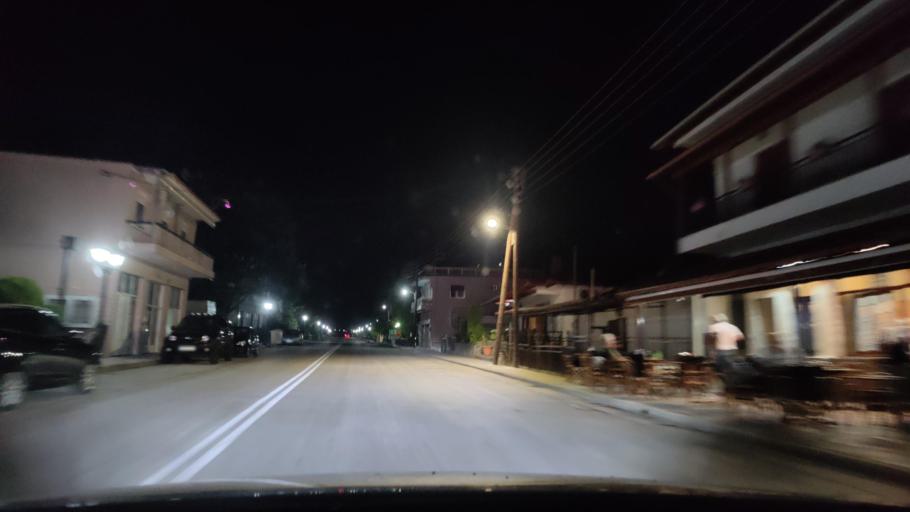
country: GR
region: Central Macedonia
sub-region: Nomos Serron
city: Neo Petritsi
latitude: 41.2651
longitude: 23.2532
